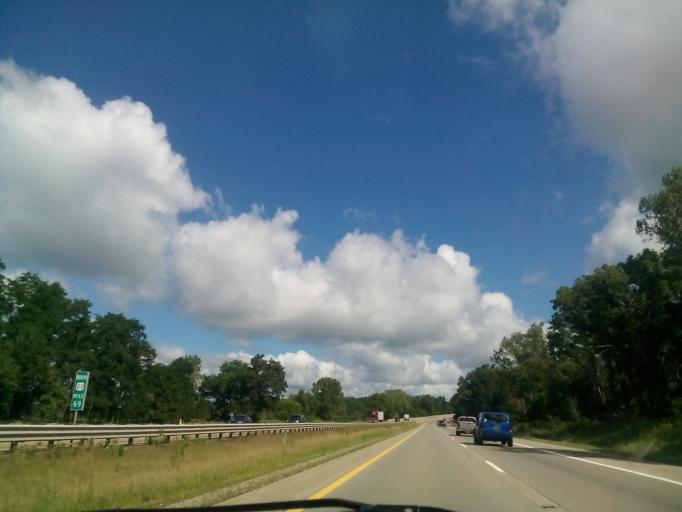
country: US
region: Michigan
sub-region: Livingston County
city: Brighton
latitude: 42.6571
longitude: -83.7580
